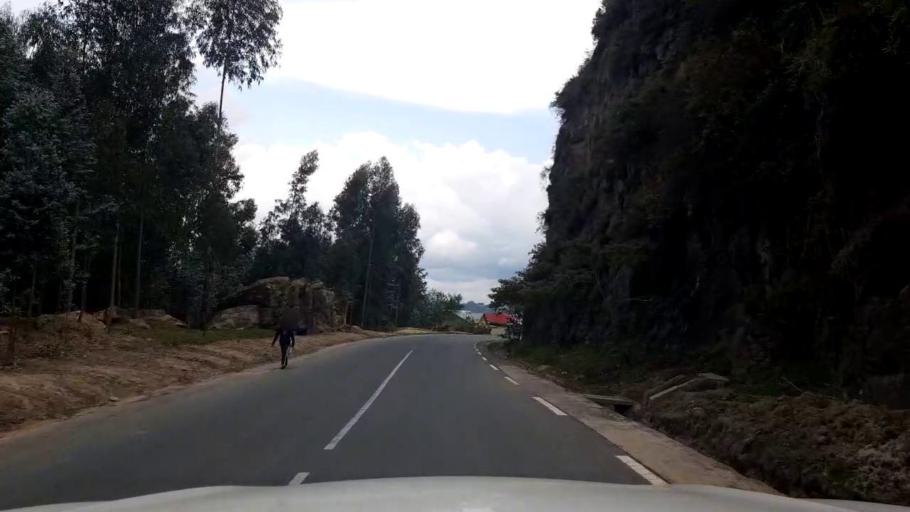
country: RW
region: Northern Province
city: Musanze
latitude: -1.6713
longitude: 29.5154
